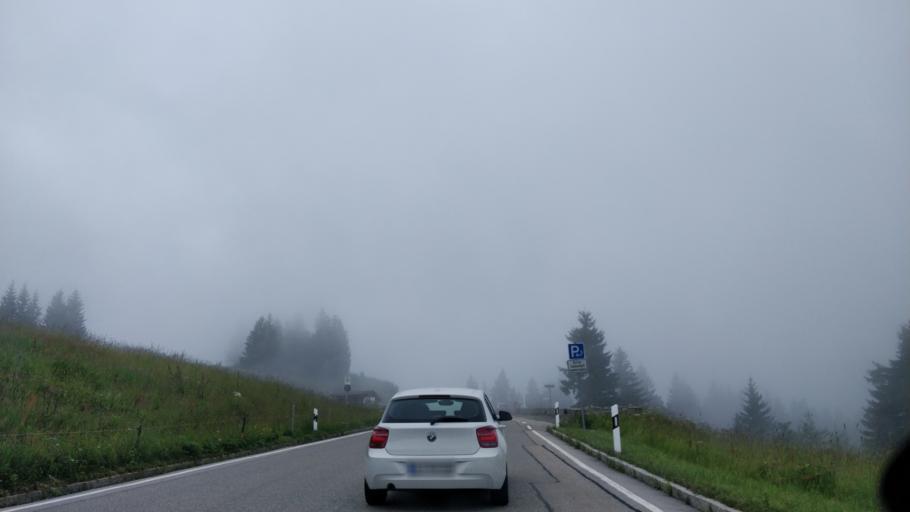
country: AT
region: Salzburg
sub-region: Politischer Bezirk Hallein
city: Kuchl
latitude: 47.6283
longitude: 13.0944
